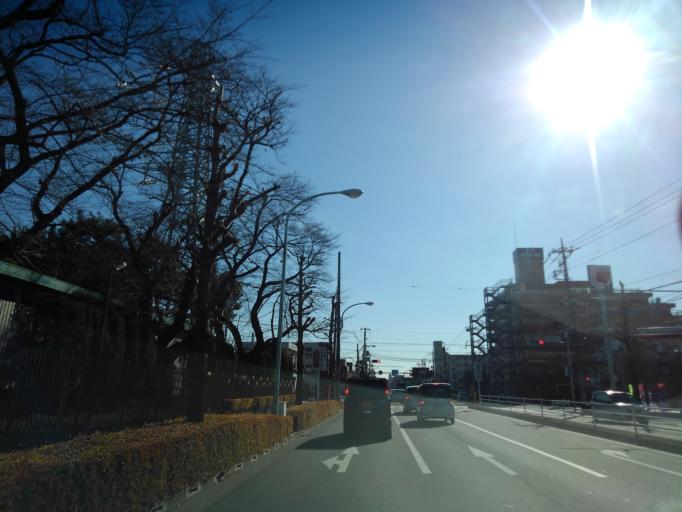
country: JP
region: Tokyo
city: Fussa
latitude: 35.7656
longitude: 139.3203
